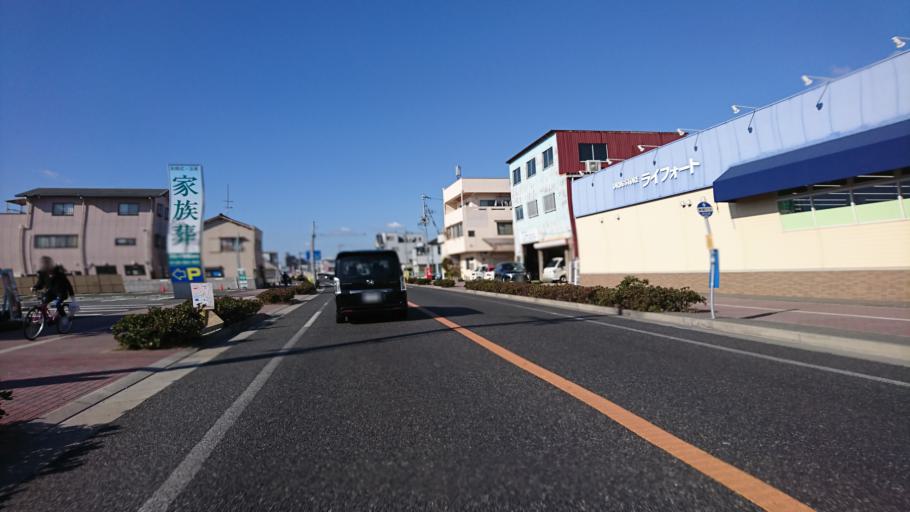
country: JP
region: Hyogo
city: Akashi
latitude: 34.6485
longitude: 134.9757
